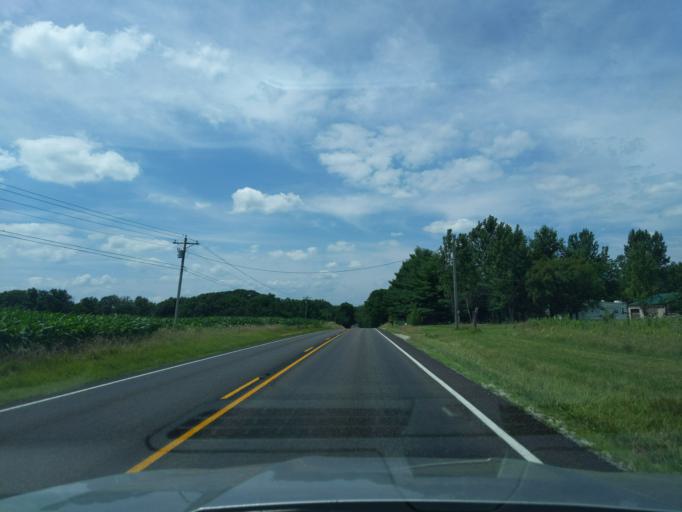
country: US
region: Indiana
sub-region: Decatur County
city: Greensburg
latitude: 39.2649
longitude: -85.3795
